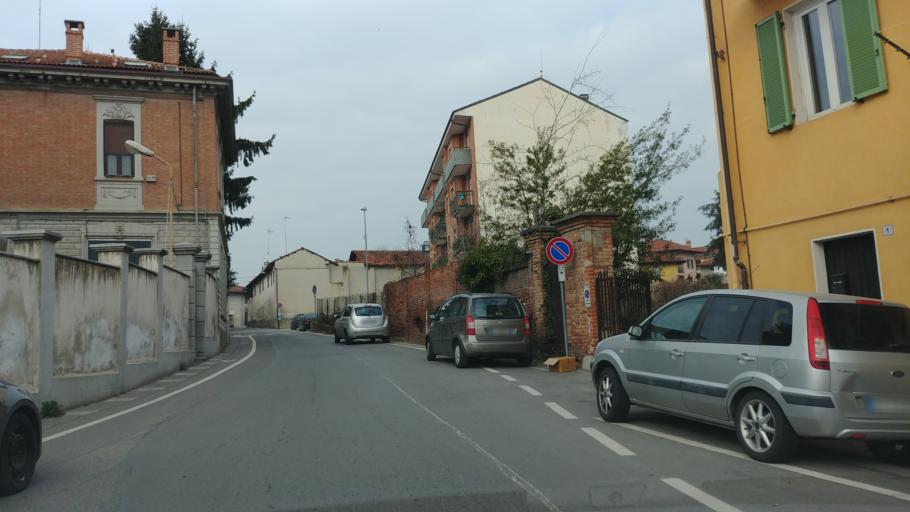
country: IT
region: Piedmont
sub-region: Provincia di Cuneo
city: Fossano
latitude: 44.5445
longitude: 7.7200
